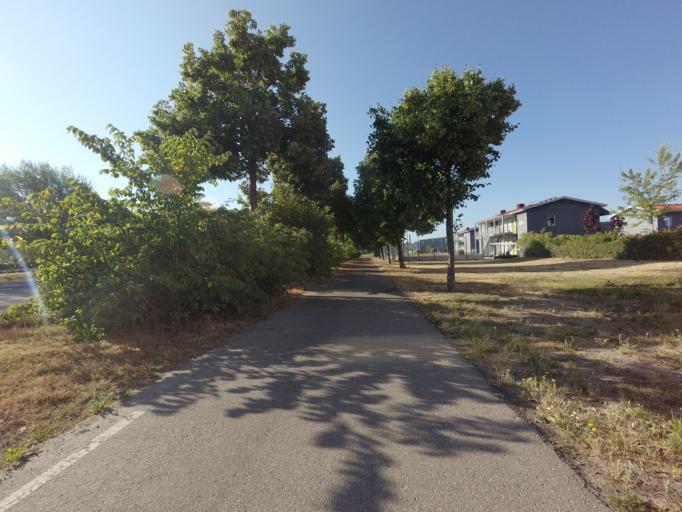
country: SE
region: Skane
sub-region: Landskrona
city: Landskrona
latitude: 55.8972
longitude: 12.8261
